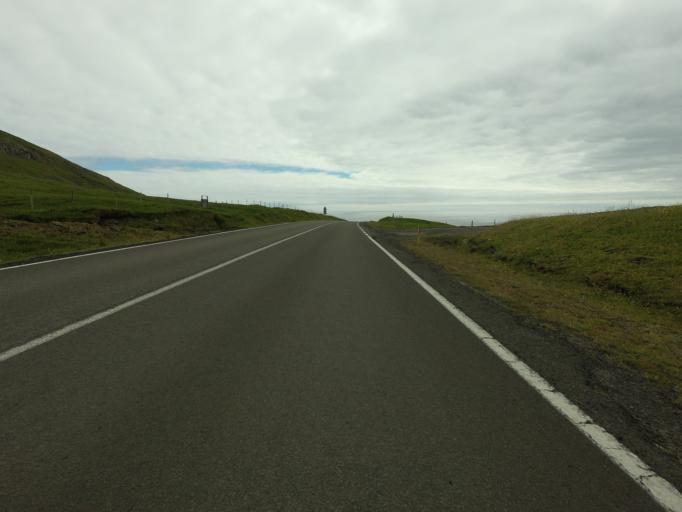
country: FO
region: Suduroy
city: Vagur
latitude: 61.4124
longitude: -6.7438
